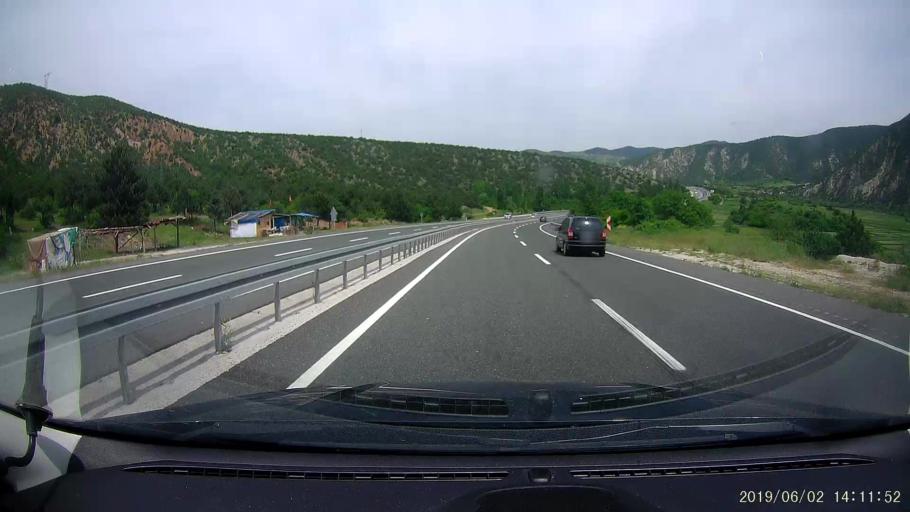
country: TR
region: Cankiri
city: Yaprakli
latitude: 40.9119
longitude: 33.7949
